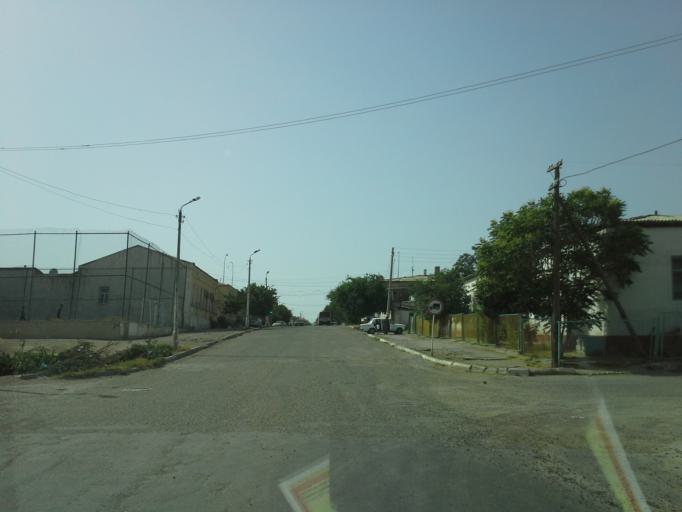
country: TM
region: Balkan
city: Turkmenbasy
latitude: 40.0077
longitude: 52.9979
